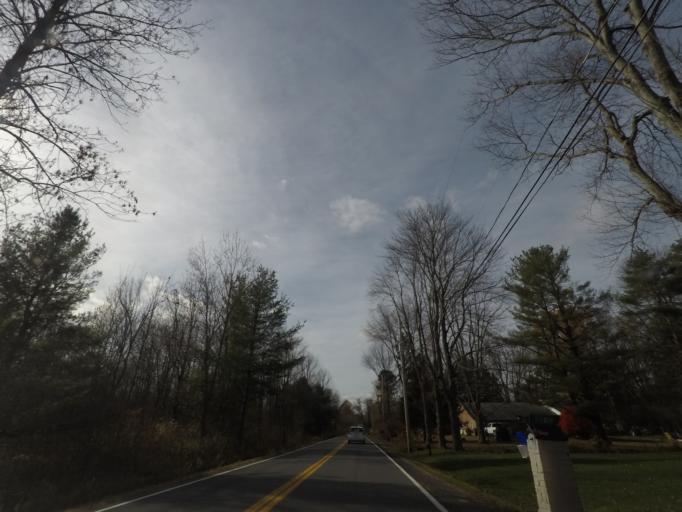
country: US
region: New York
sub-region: Schenectady County
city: Rotterdam
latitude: 42.7546
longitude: -73.9798
